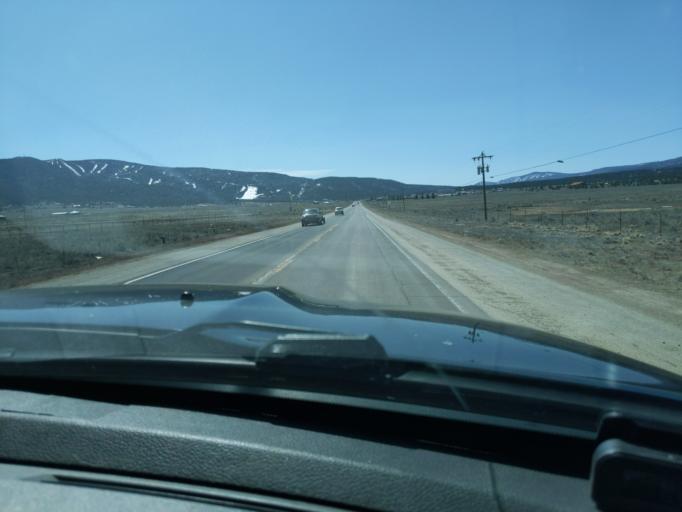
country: US
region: New Mexico
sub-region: Colfax County
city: Angel Fire
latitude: 36.4211
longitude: -105.2969
